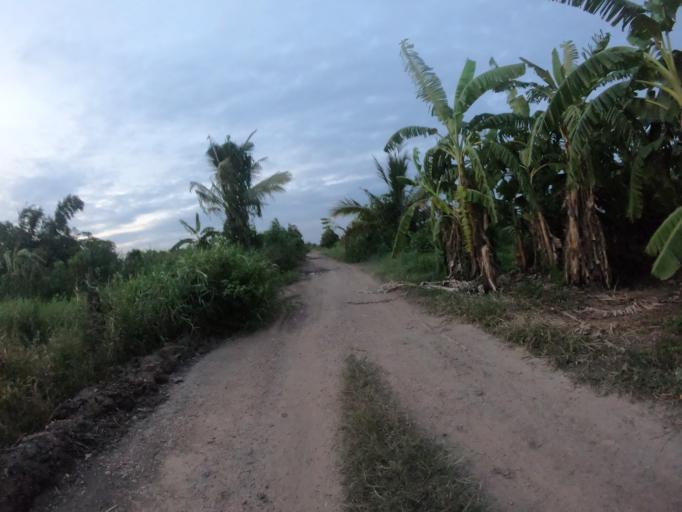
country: TH
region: Pathum Thani
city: Ban Rangsit
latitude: 14.0254
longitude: 100.8019
